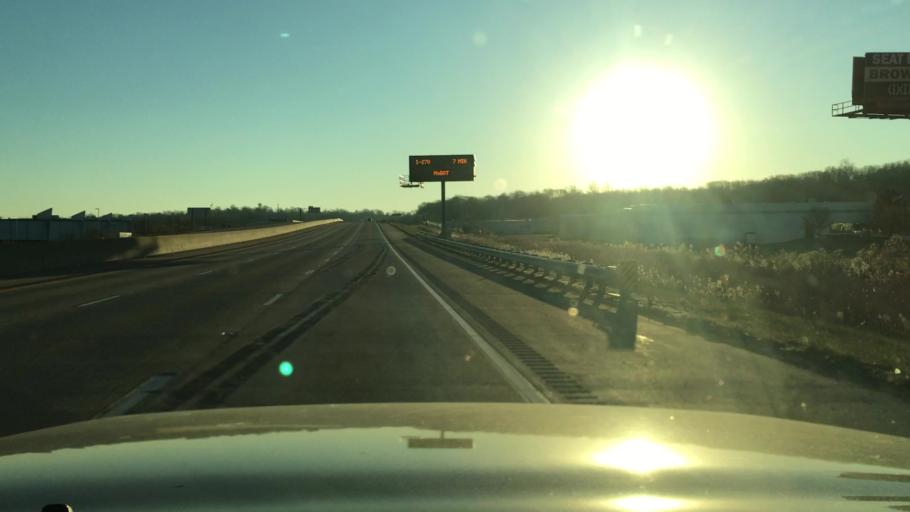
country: US
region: Missouri
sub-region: Saint Charles County
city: Saint Charles
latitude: 38.8221
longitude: -90.5107
